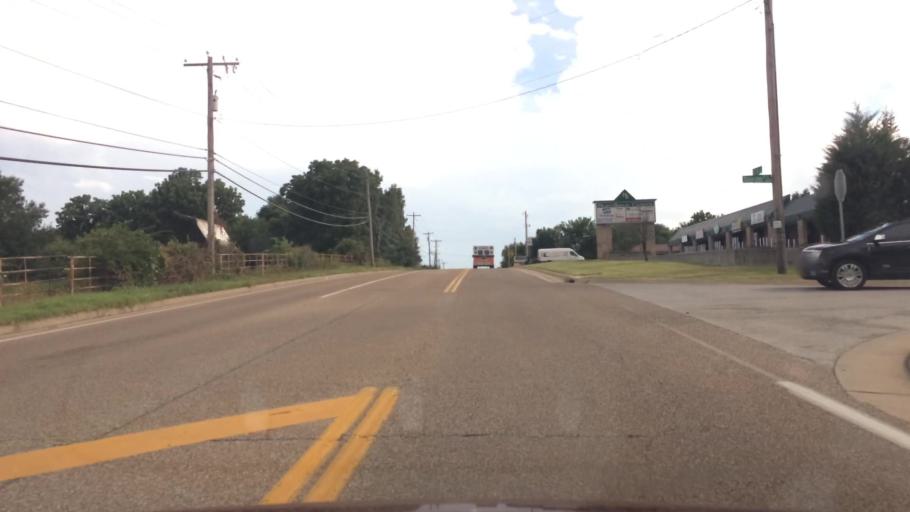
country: US
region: Missouri
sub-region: Greene County
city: Springfield
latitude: 37.2663
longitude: -93.2647
